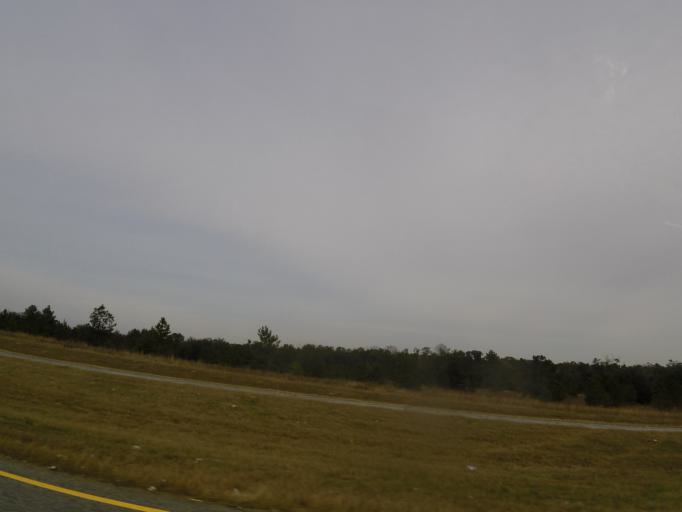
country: US
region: Georgia
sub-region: Seminole County
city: Donalsonville
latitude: 30.9809
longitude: -84.7541
